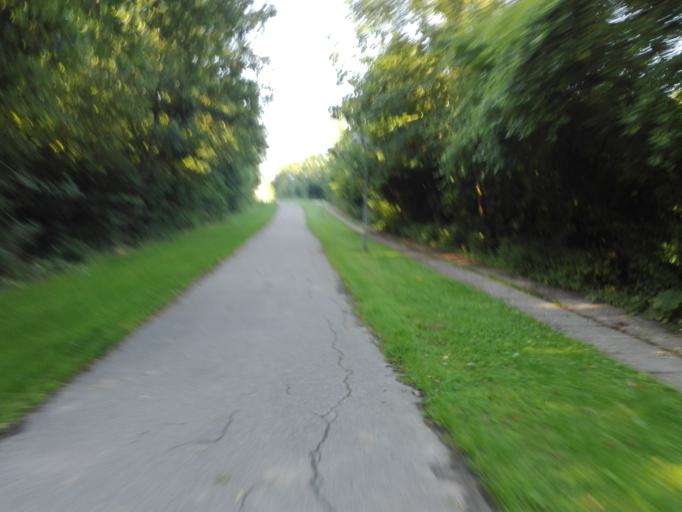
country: DK
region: Central Jutland
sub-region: Arhus Kommune
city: Tranbjerg
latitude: 56.0849
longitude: 10.1430
